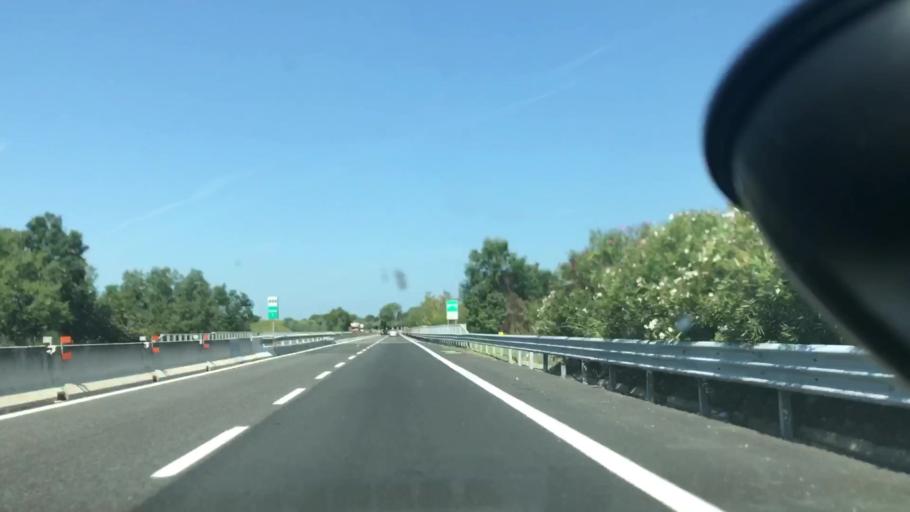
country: IT
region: Abruzzo
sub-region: Provincia di Chieti
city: Tollo
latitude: 42.3533
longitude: 14.3527
